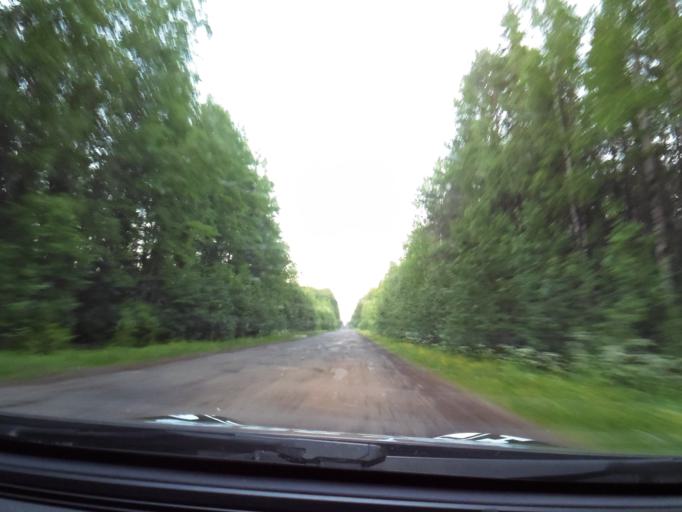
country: RU
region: Leningrad
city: Voznesen'ye
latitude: 60.8360
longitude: 35.6605
